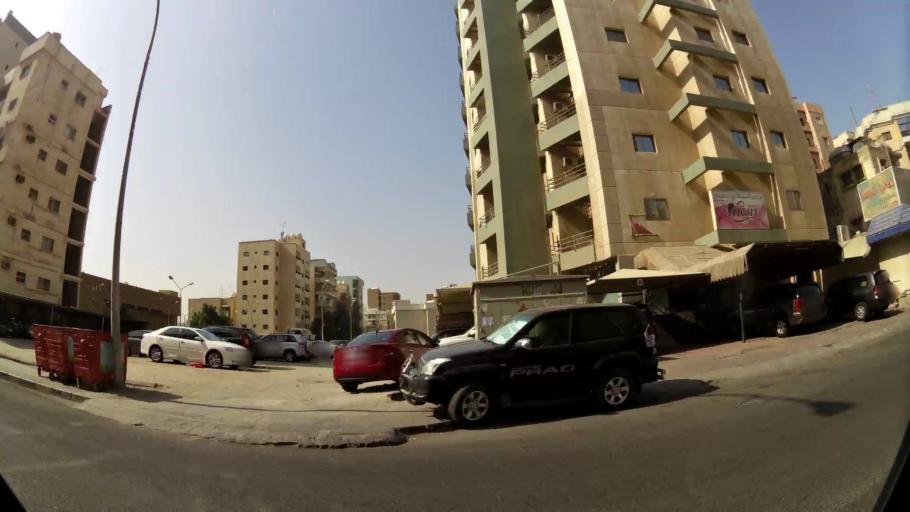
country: KW
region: Muhafazat Hawalli
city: Hawalli
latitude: 29.3369
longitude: 48.0122
